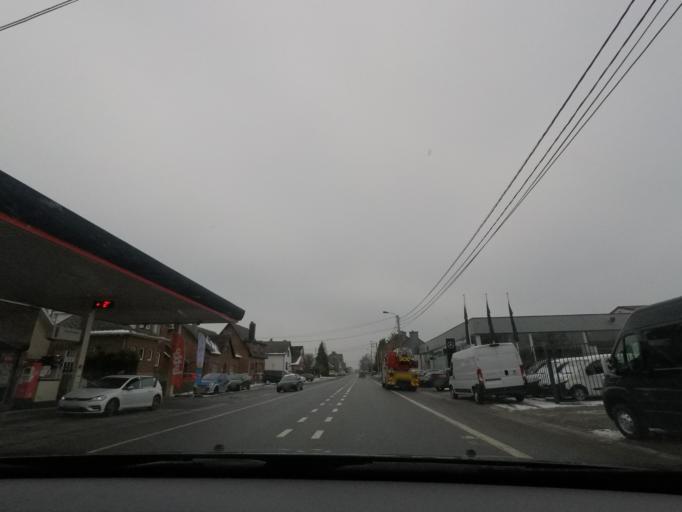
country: BE
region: Wallonia
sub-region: Province de Namur
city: Fosses-la-Ville
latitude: 50.4716
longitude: 4.6714
